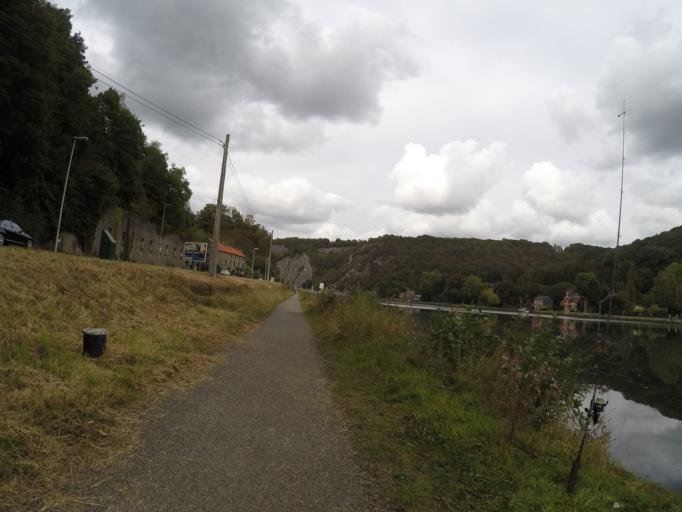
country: BE
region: Wallonia
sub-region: Province de Namur
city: Yvoir
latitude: 50.3313
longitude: 4.8715
